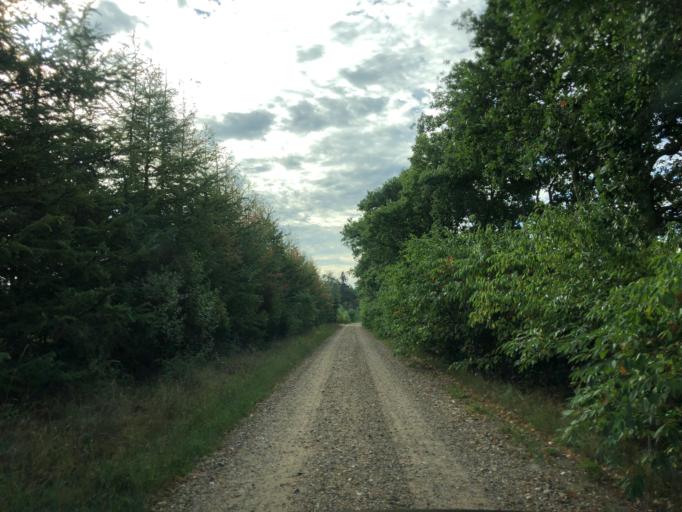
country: DK
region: Central Jutland
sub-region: Holstebro Kommune
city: Ulfborg
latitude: 56.1855
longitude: 8.3449
